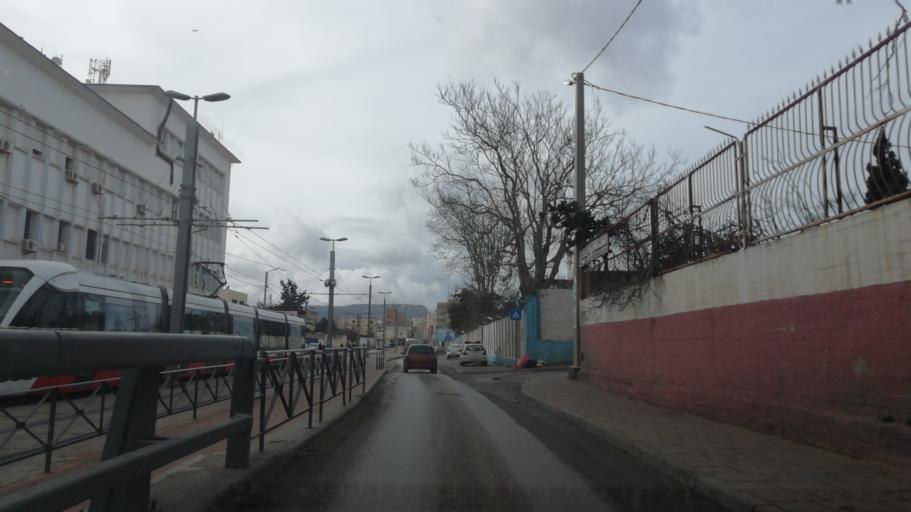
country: DZ
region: Oran
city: Oran
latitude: 35.6975
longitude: -0.6150
